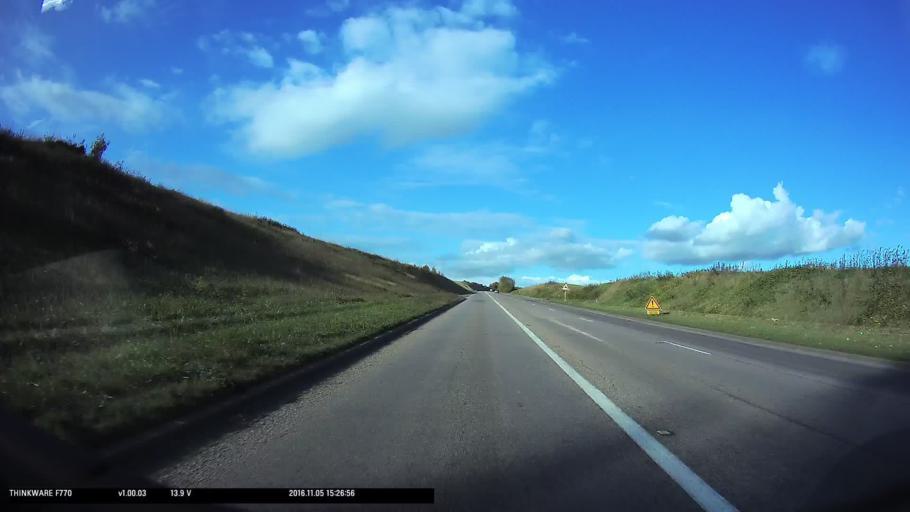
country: FR
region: Ile-de-France
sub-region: Departement des Yvelines
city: Meulan-en-Yvelines
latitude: 49.0176
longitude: 1.9101
